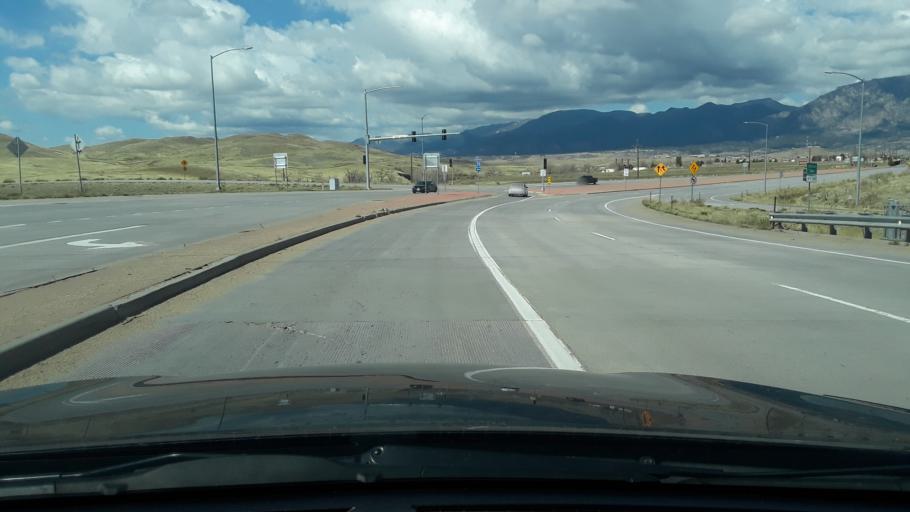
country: US
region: Colorado
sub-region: El Paso County
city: Security-Widefield
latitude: 38.7249
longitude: -104.7339
